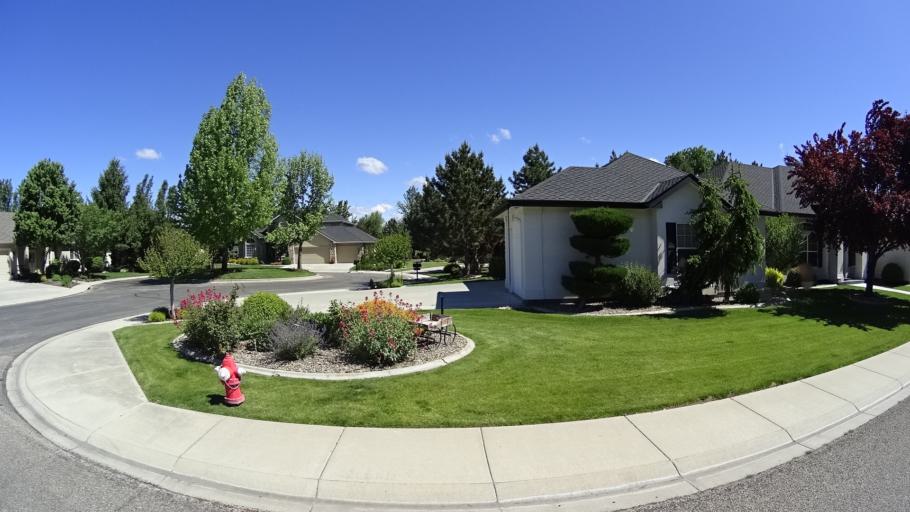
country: US
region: Idaho
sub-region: Ada County
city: Eagle
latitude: 43.6692
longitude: -116.3588
